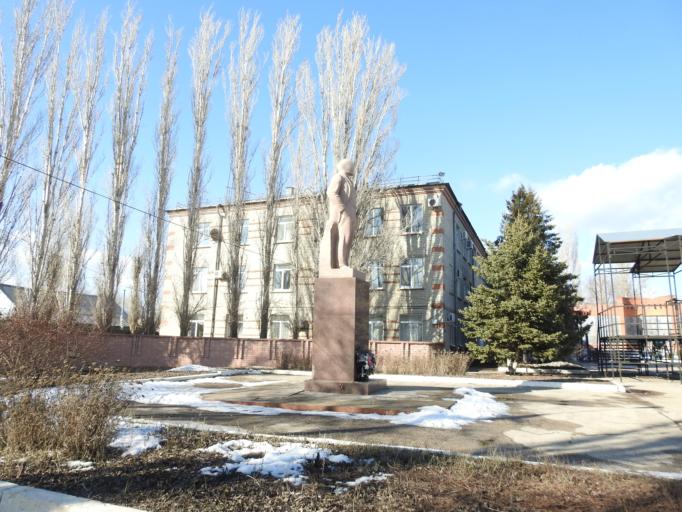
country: RU
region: Saratov
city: Yershov
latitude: 51.3496
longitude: 48.2652
